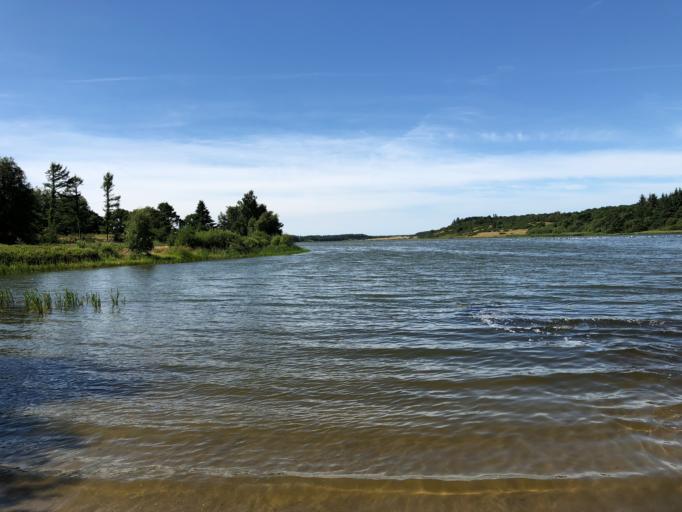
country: DK
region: Central Jutland
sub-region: Holstebro Kommune
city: Vinderup
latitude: 56.4203
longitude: 8.9356
